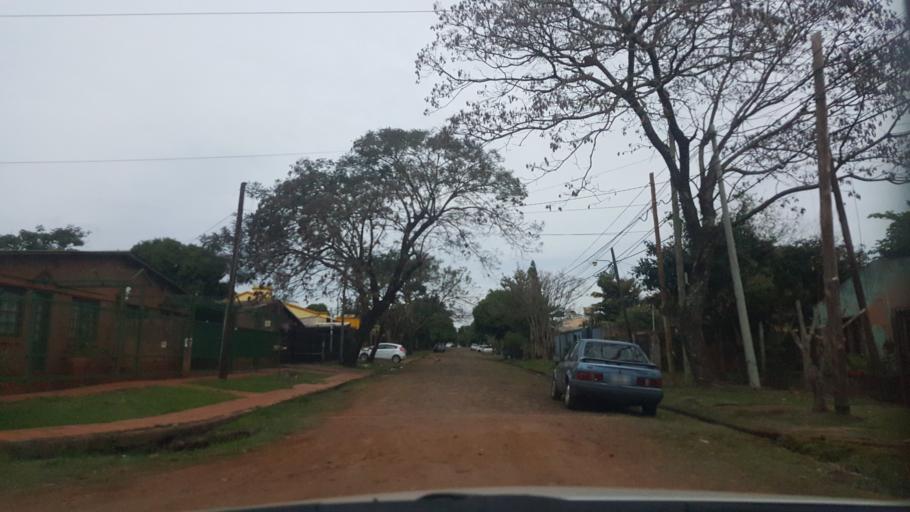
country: AR
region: Misiones
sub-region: Departamento de Capital
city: Posadas
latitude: -27.3827
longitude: -55.9215
